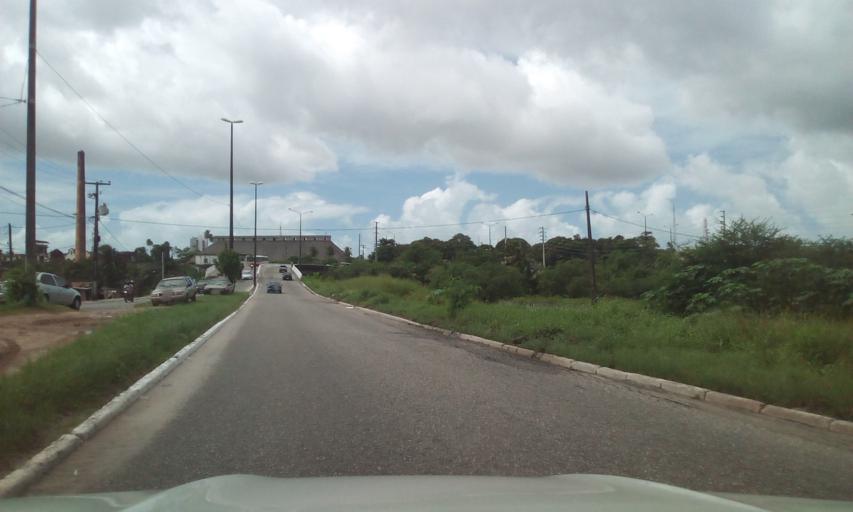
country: BR
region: Paraiba
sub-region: Joao Pessoa
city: Joao Pessoa
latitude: -7.1238
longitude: -34.8960
